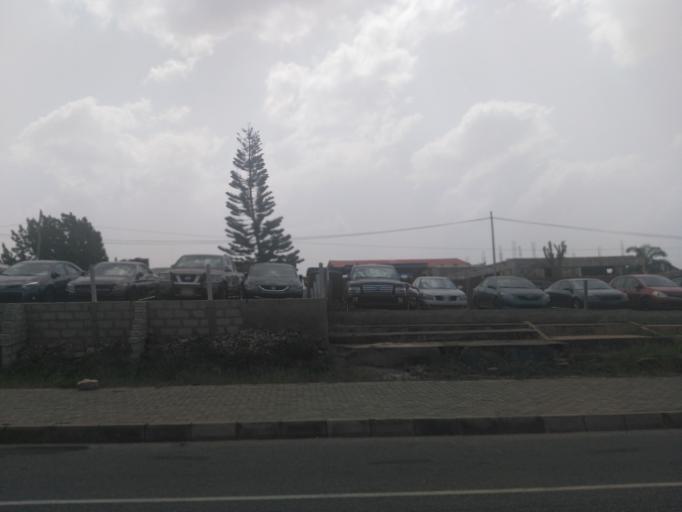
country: GH
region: Greater Accra
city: Dome
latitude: 5.6142
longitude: -0.2211
